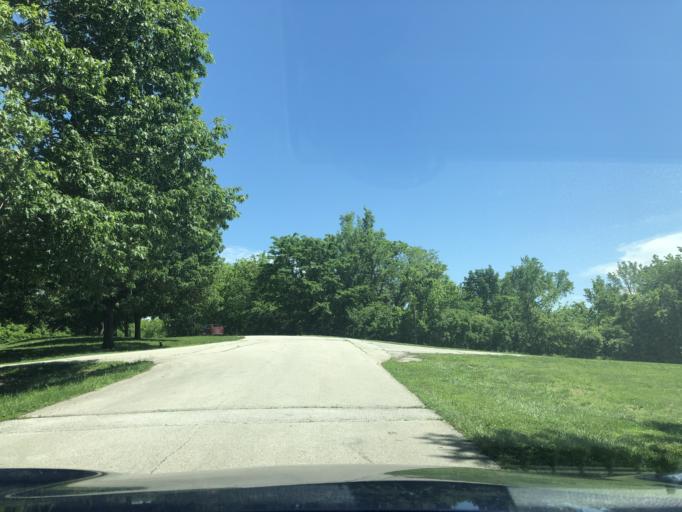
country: US
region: Missouri
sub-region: Platte County
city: Weston
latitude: 39.3919
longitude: -94.8741
